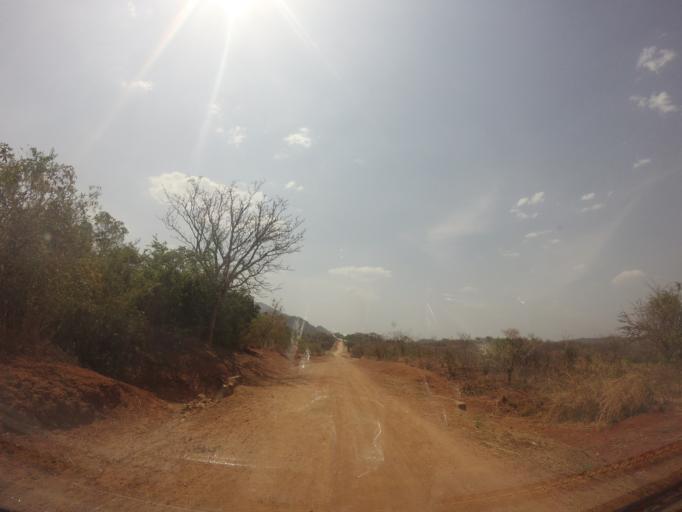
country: UG
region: Northern Region
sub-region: Arua District
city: Arua
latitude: 2.8968
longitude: 31.1187
